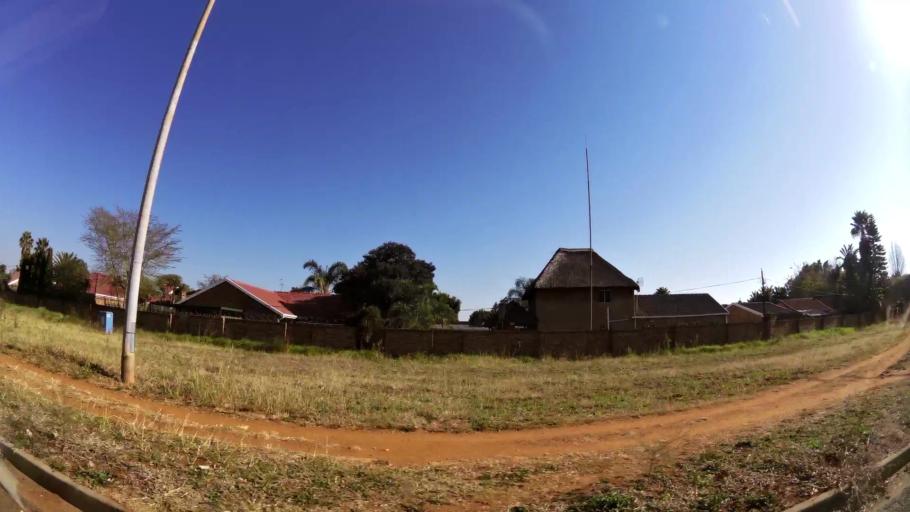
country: ZA
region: Gauteng
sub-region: City of Johannesburg Metropolitan Municipality
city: Modderfontein
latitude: -26.0548
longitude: 28.2045
